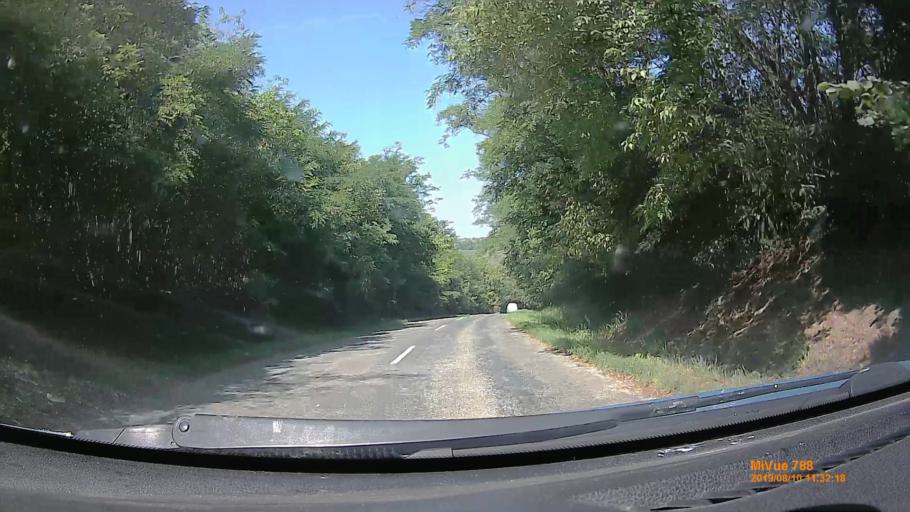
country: HU
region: Somogy
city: Somogyvar
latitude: 46.5247
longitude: 17.7920
